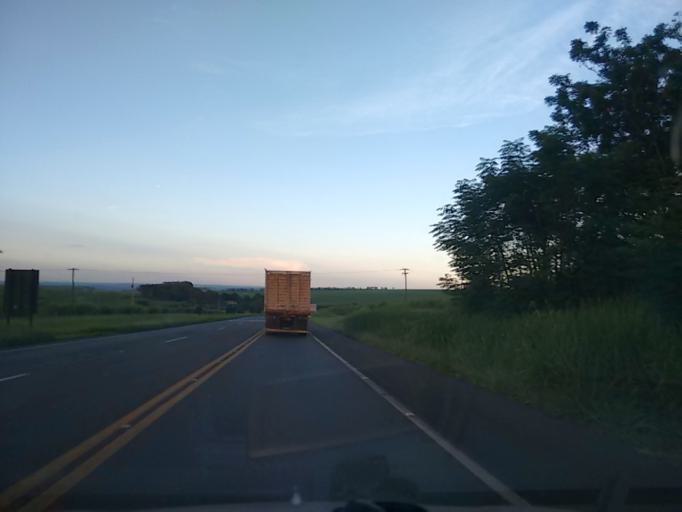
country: BR
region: Sao Paulo
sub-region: Jau
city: Jau
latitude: -22.1518
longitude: -48.4706
